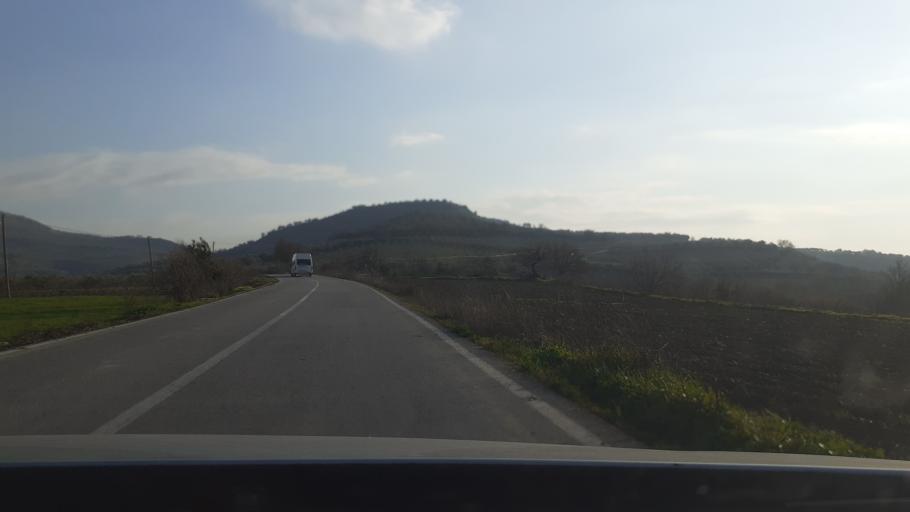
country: TR
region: Hatay
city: Oymakli
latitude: 36.1271
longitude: 36.3096
